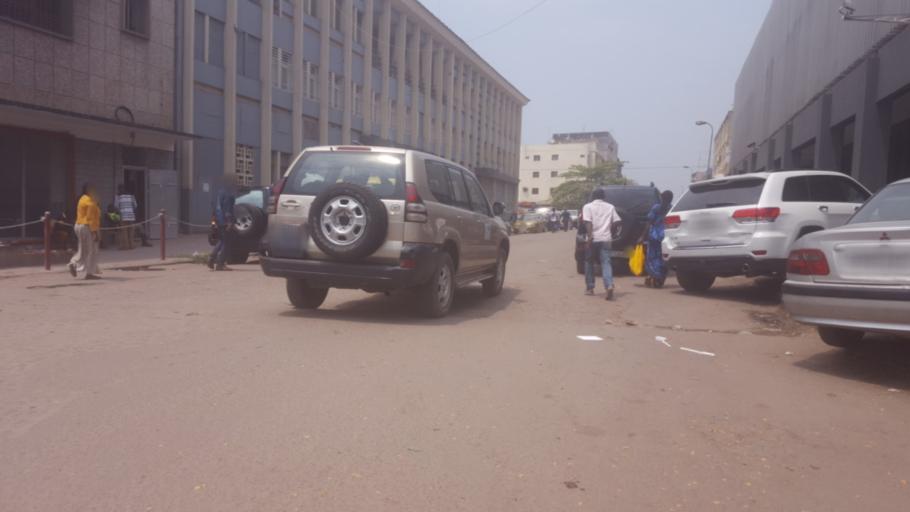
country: CD
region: Kinshasa
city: Kinshasa
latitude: -4.3068
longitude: 15.3095
